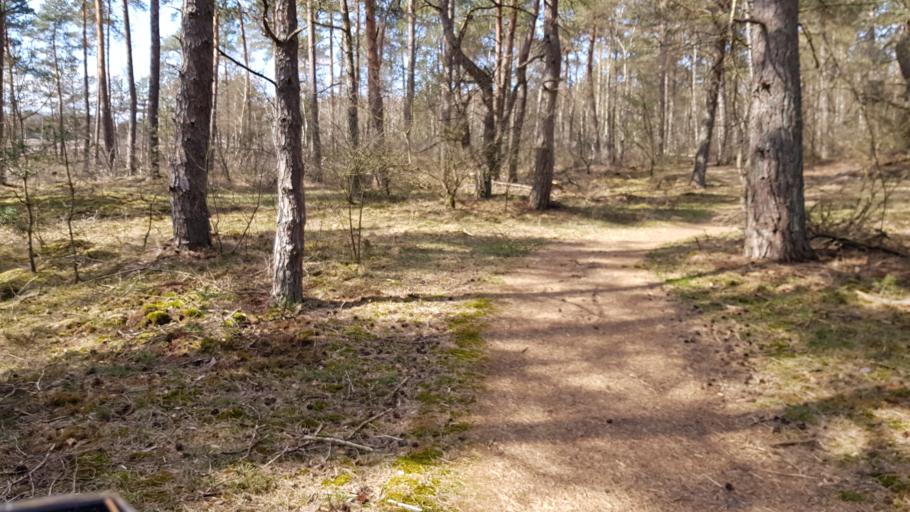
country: NL
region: Gelderland
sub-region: Gemeente Apeldoorn
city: Loenen
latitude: 52.0826
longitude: 6.0152
